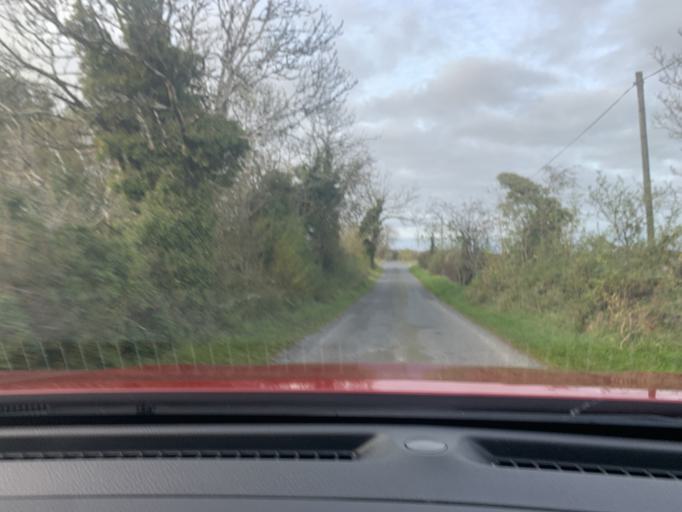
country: IE
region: Connaught
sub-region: Roscommon
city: Ballaghaderreen
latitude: 53.9999
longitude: -8.6068
